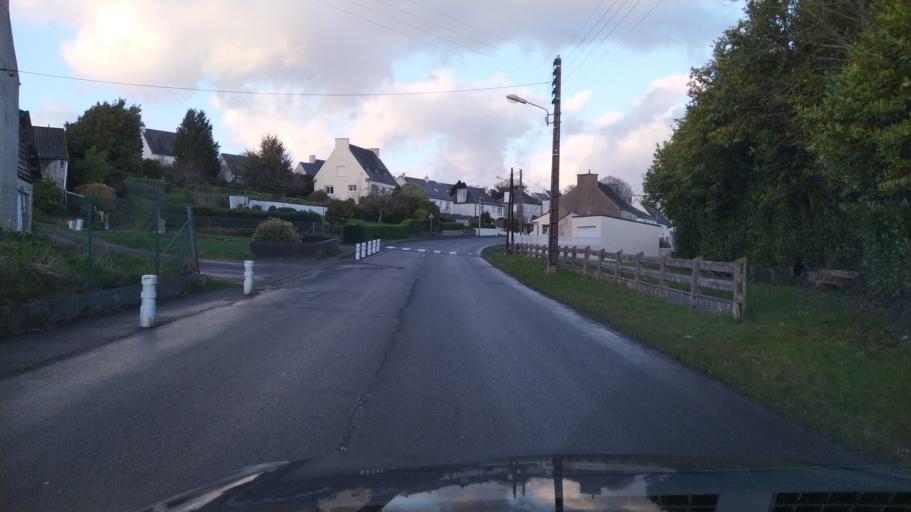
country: FR
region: Brittany
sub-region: Departement du Finistere
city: Landivisiau
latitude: 48.4985
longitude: -4.0756
